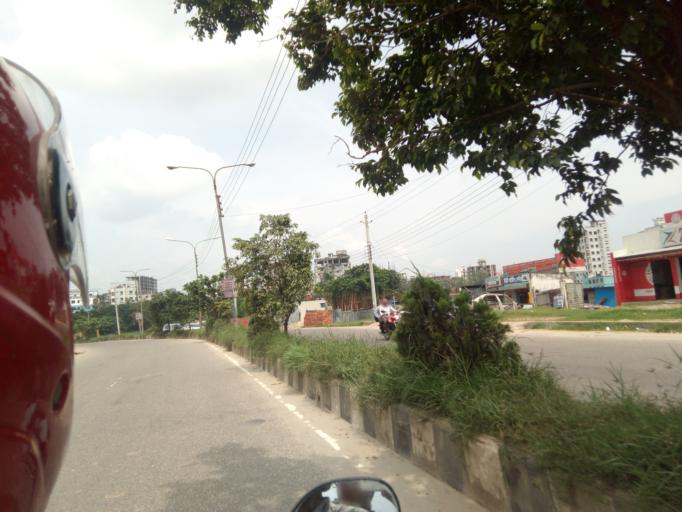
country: BD
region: Dhaka
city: Tungi
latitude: 23.8202
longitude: 90.3896
